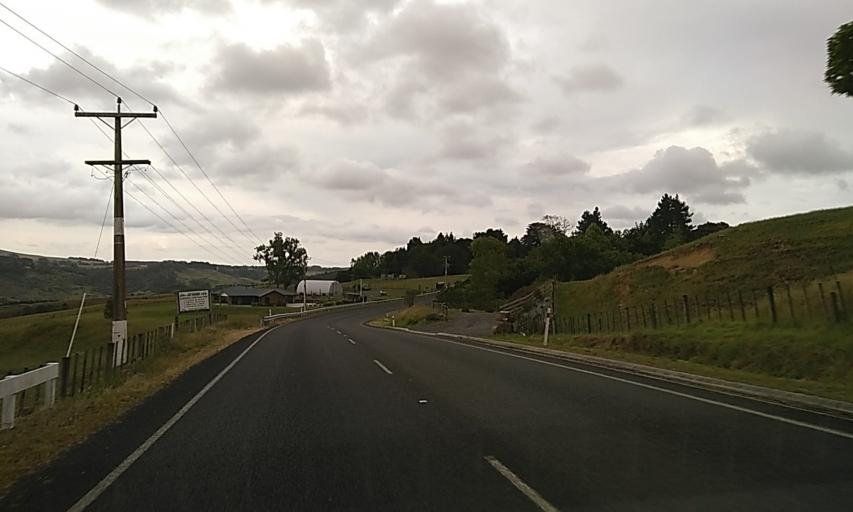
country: NZ
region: Auckland
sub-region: Auckland
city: Pukekohe East
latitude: -37.3106
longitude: 174.9376
